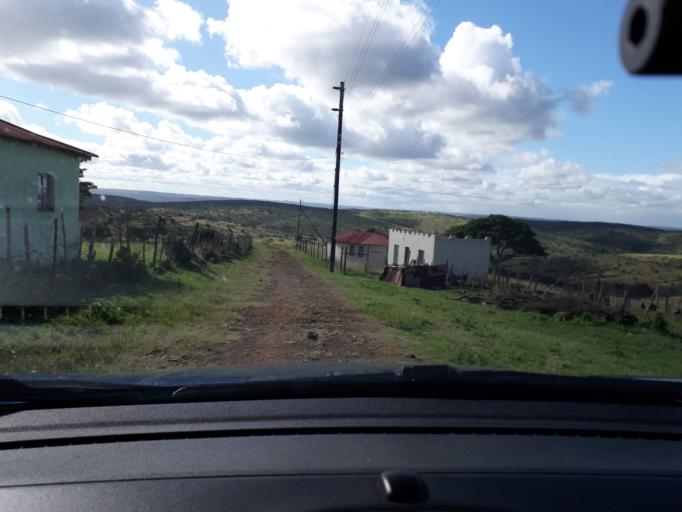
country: ZA
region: Eastern Cape
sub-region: Buffalo City Metropolitan Municipality
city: Bhisho
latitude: -33.1096
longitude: 27.4290
